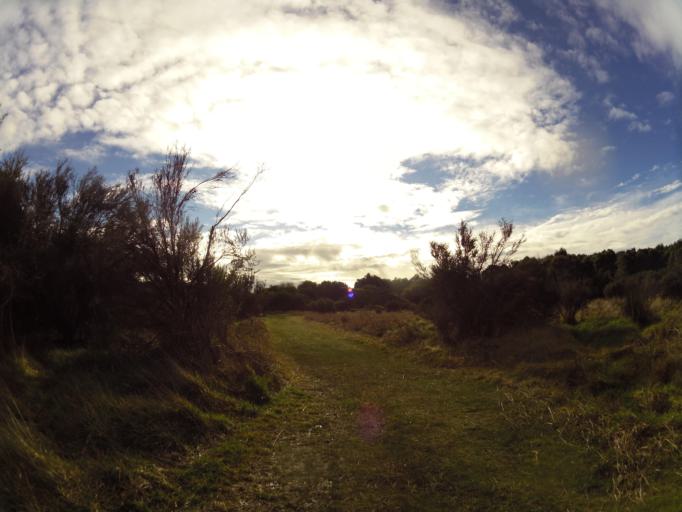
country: AU
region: Victoria
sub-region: Bass Coast
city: North Wonthaggi
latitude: -38.6232
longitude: 145.5734
